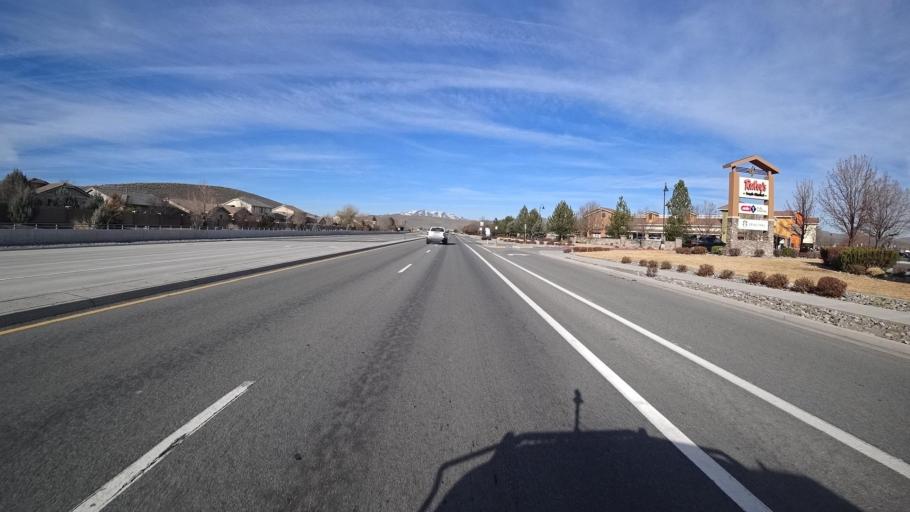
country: US
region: Nevada
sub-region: Washoe County
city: Spanish Springs
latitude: 39.6070
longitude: -119.6977
